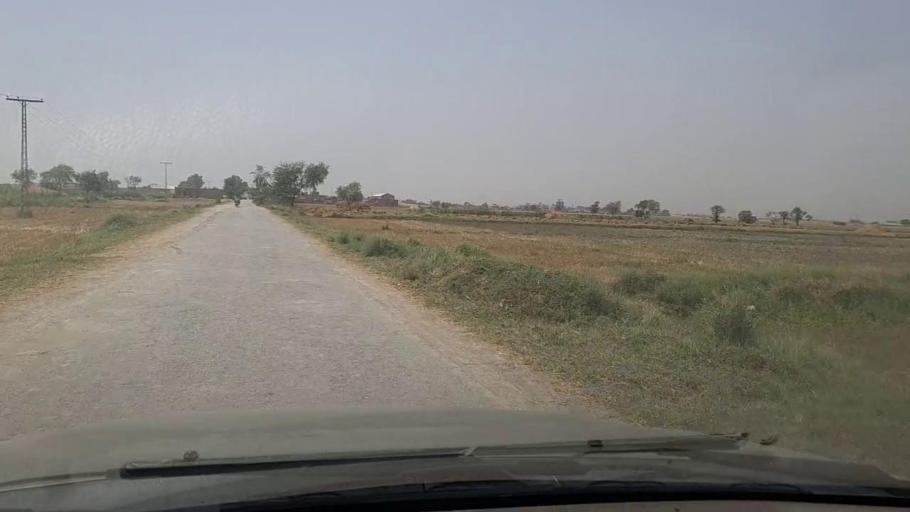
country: PK
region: Sindh
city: Miro Khan
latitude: 27.7622
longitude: 68.1116
